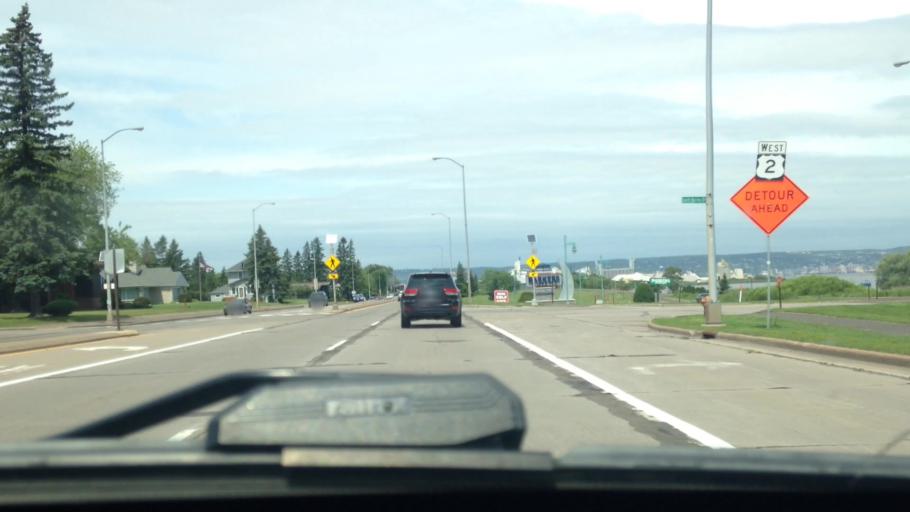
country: US
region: Wisconsin
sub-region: Douglas County
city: Superior
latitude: 46.7185
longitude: -92.0627
